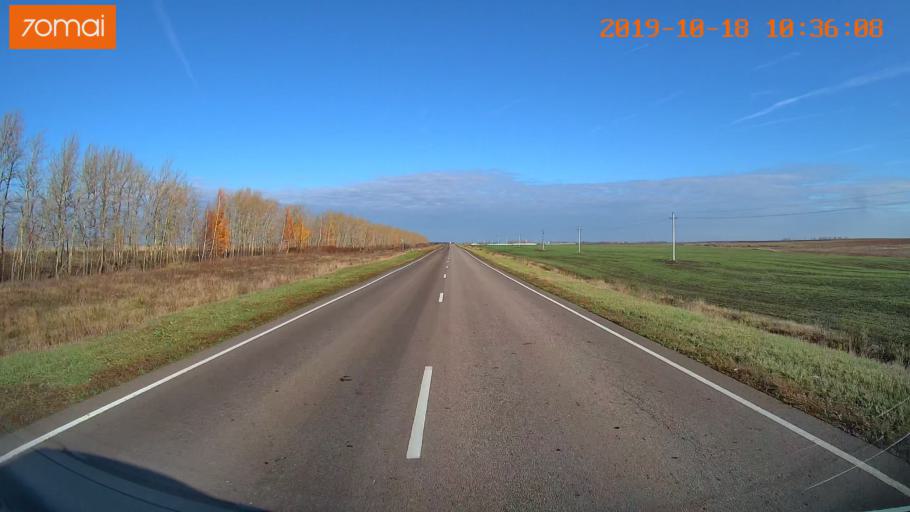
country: RU
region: Tula
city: Kurkino
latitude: 53.5436
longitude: 38.6238
